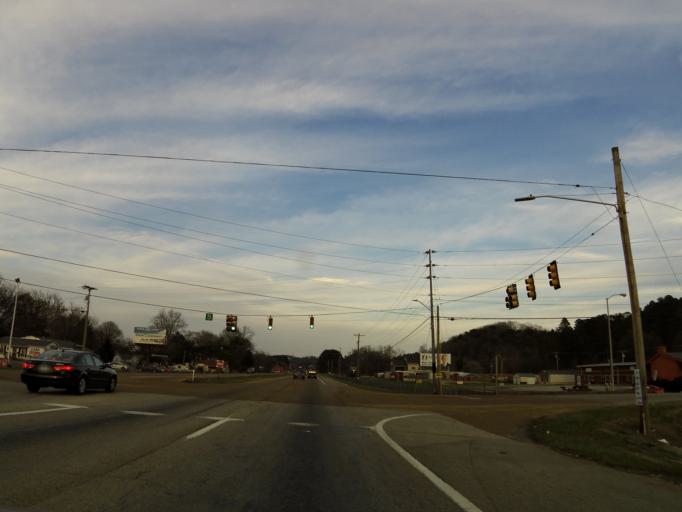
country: US
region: Tennessee
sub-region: Rhea County
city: Dayton
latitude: 35.4824
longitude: -85.0224
